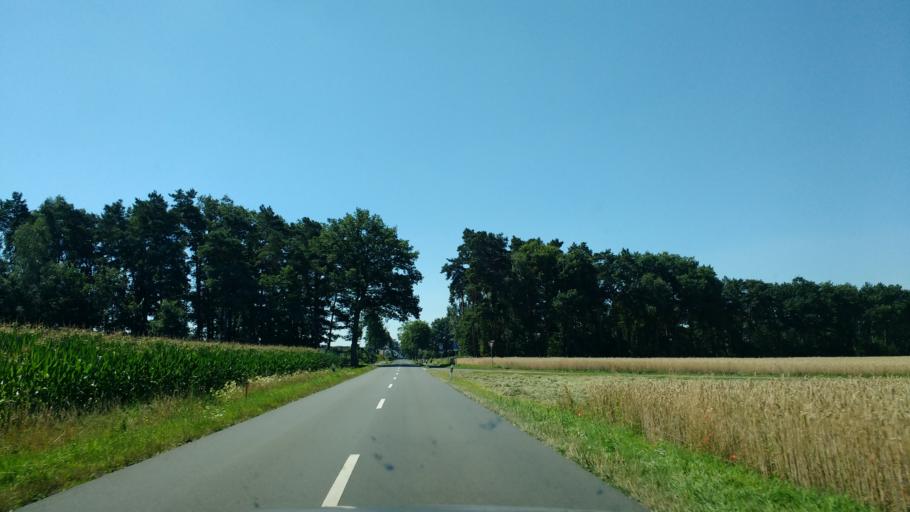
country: DE
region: North Rhine-Westphalia
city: Geseke
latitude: 51.7150
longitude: 8.4923
